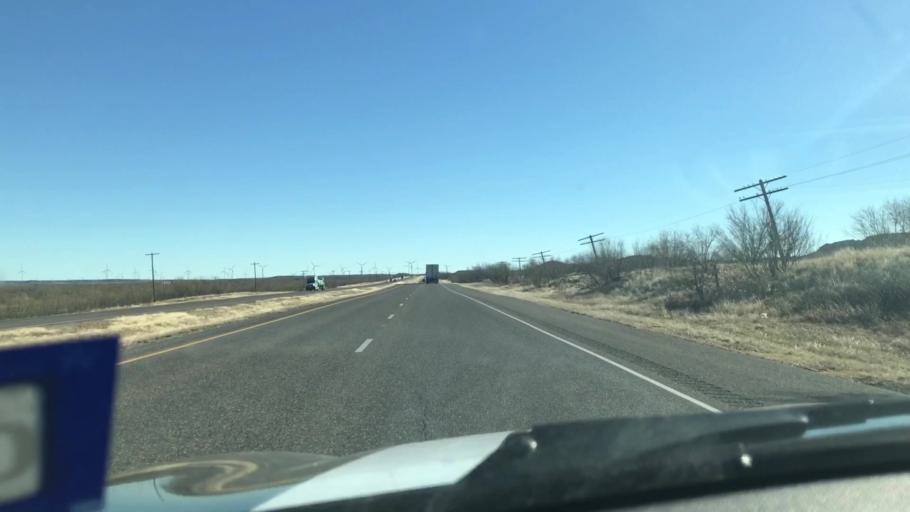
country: US
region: Texas
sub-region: Scurry County
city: Snyder
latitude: 32.9553
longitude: -101.0875
